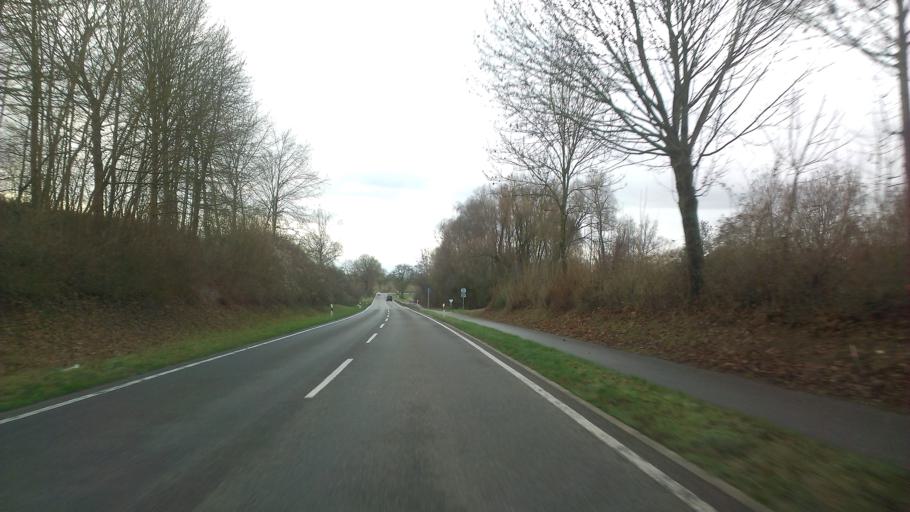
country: DE
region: Baden-Wuerttemberg
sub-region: Karlsruhe Region
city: Ubstadt-Weiher
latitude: 49.1299
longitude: 8.6977
